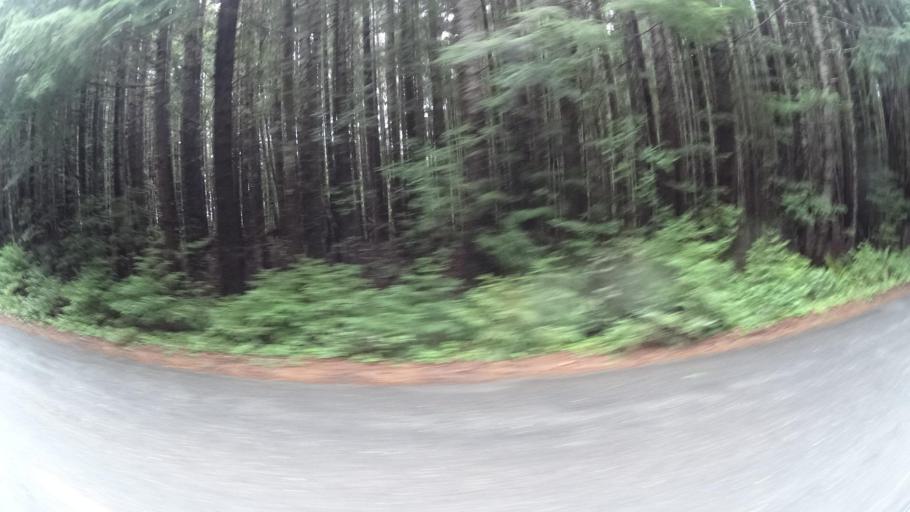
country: US
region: California
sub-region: Humboldt County
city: Westhaven-Moonstone
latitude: 41.2402
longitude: -123.9828
